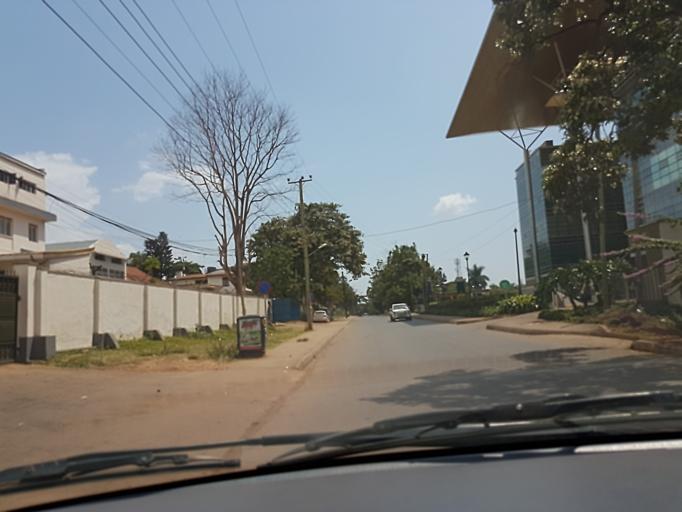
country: UG
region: Central Region
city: Kampala Central Division
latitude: 0.3223
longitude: 32.5775
